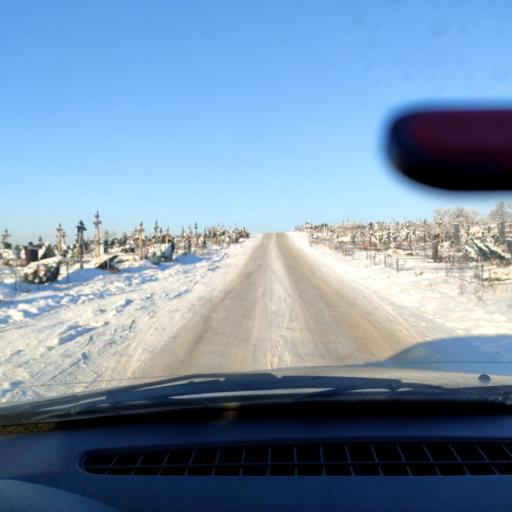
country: RU
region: Bashkortostan
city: Ufa
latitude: 54.8563
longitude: 56.1659
